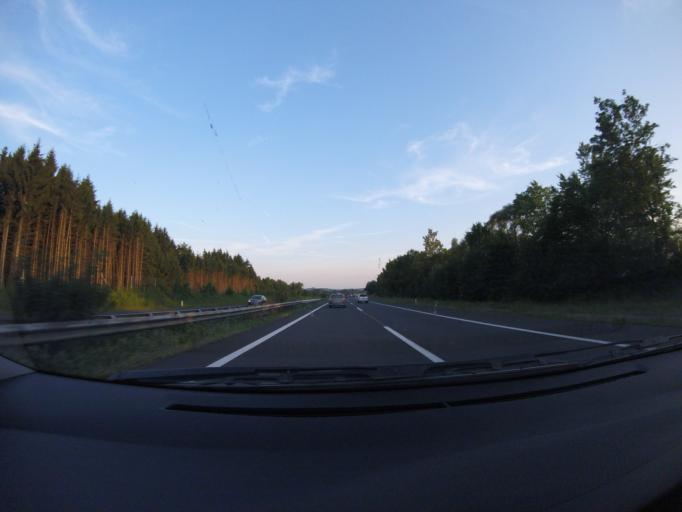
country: AT
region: Styria
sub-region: Politischer Bezirk Hartberg-Fuerstenfeld
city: Hainersdorf
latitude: 47.1050
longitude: 15.9849
